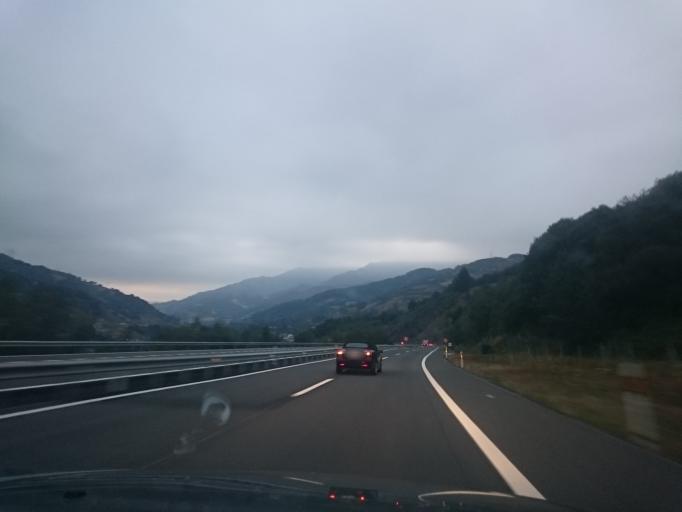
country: ES
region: Asturias
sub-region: Province of Asturias
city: Pola de Lena
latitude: 43.0969
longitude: -5.8215
